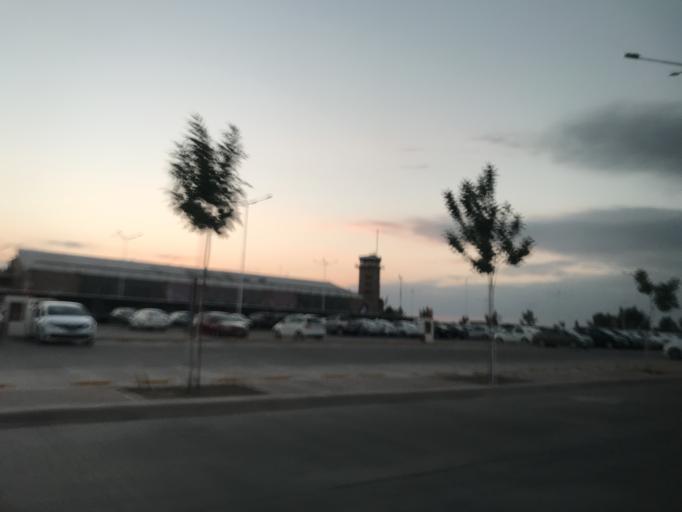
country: AR
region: Mendoza
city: Las Heras
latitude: -32.8271
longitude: -68.8003
